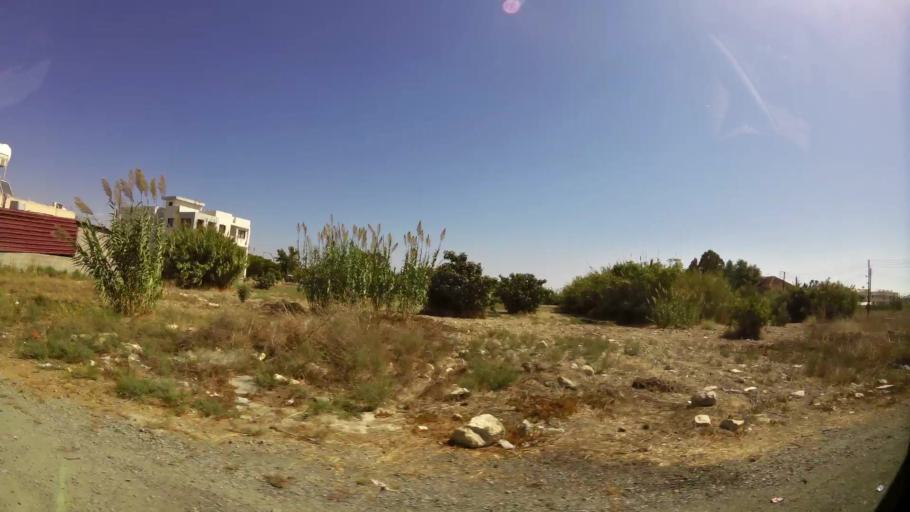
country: CY
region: Larnaka
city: Livadia
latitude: 34.9550
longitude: 33.6312
